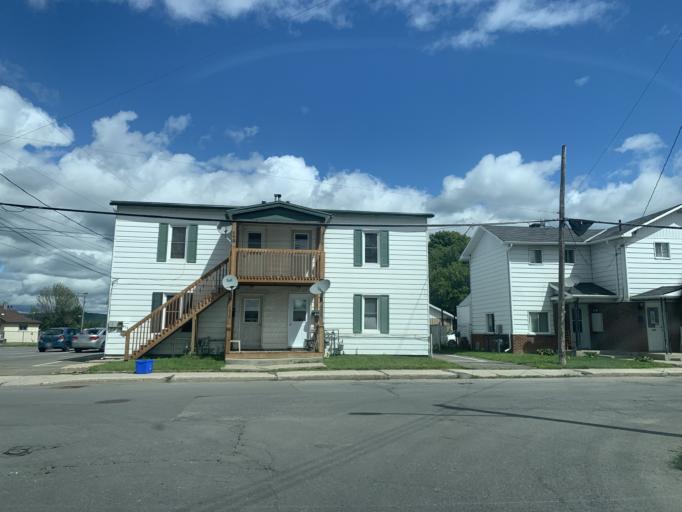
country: CA
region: Ontario
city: Hawkesbury
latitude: 45.6097
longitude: -74.5961
